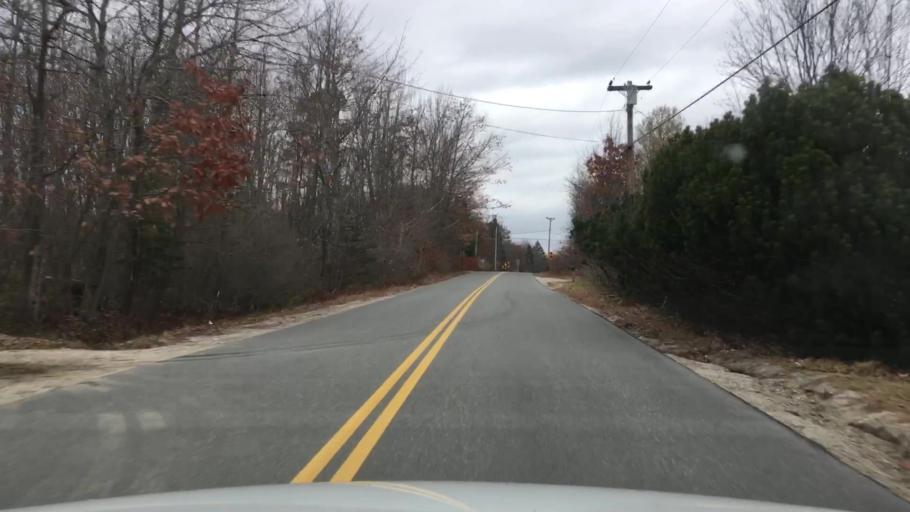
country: US
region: Maine
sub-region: Hancock County
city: Penobscot
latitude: 44.4615
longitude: -68.6374
